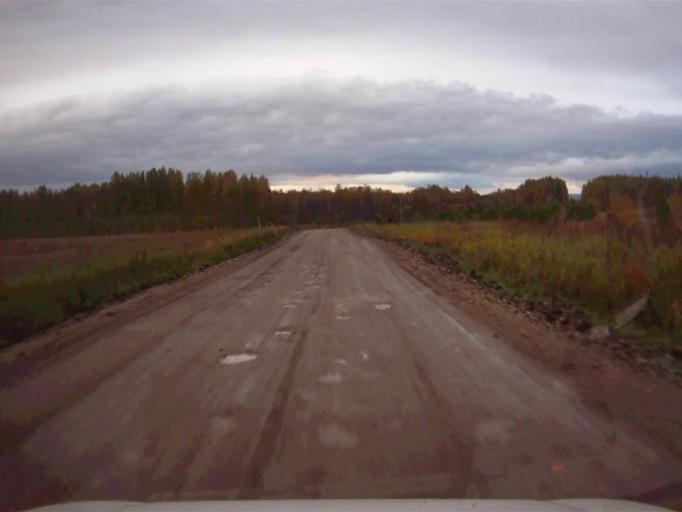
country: RU
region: Sverdlovsk
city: Mikhaylovsk
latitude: 56.1895
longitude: 59.1883
